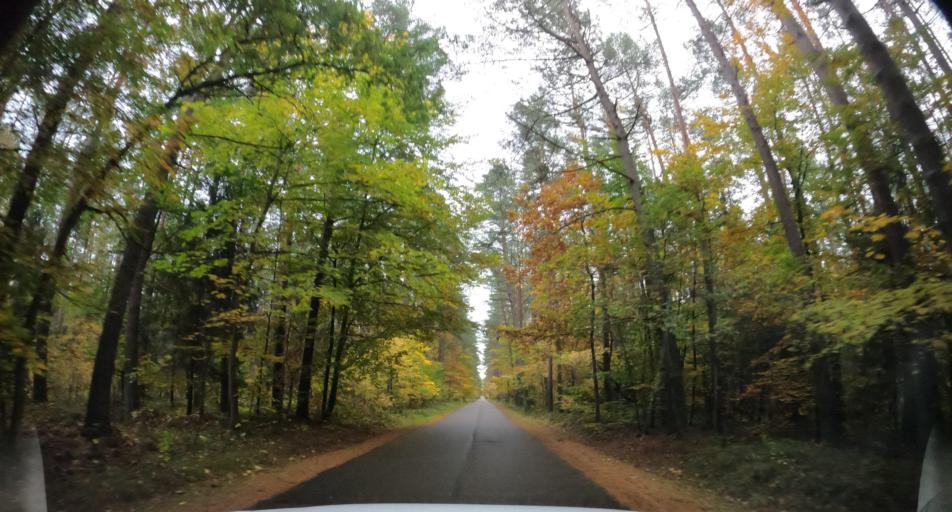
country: PL
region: West Pomeranian Voivodeship
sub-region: Powiat kamienski
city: Wolin
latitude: 53.9135
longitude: 14.5644
